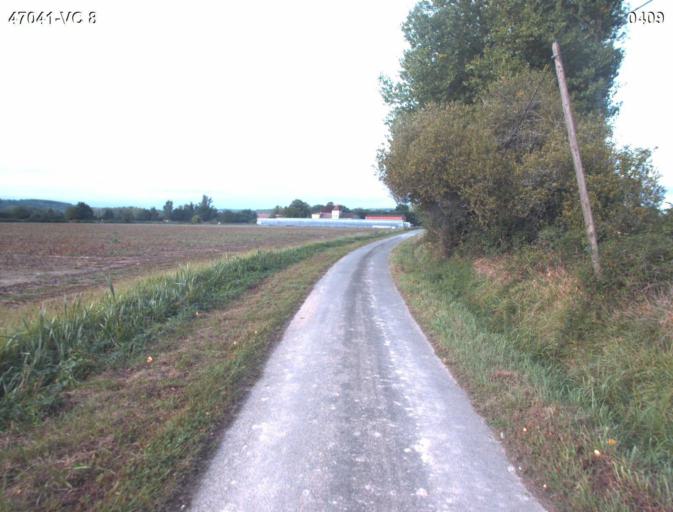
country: FR
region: Aquitaine
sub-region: Departement du Lot-et-Garonne
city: Port-Sainte-Marie
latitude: 44.2200
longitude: 0.4292
